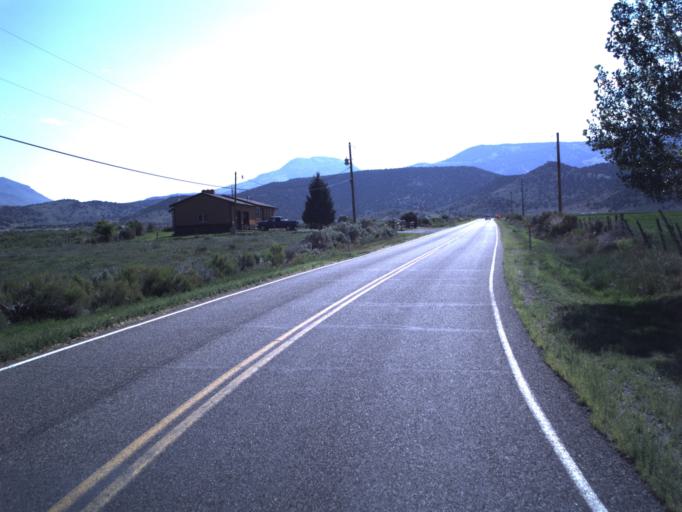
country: US
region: Utah
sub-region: Wayne County
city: Loa
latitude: 38.4693
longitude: -111.5922
